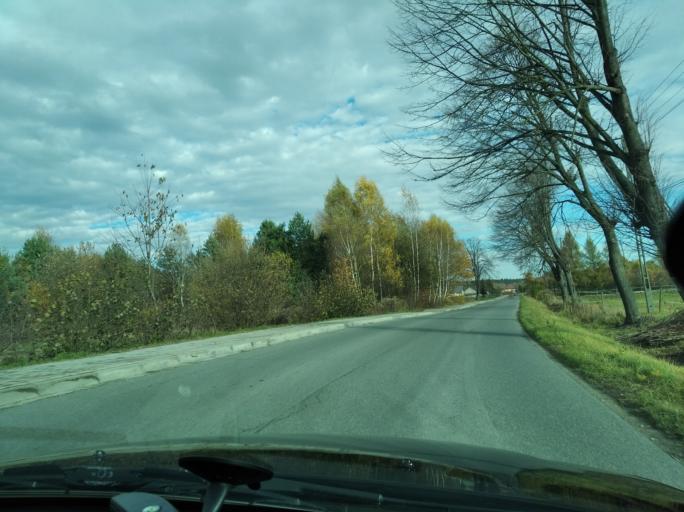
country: PL
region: Subcarpathian Voivodeship
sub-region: Powiat debicki
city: Brzeznica
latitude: 50.0941
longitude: 21.5321
